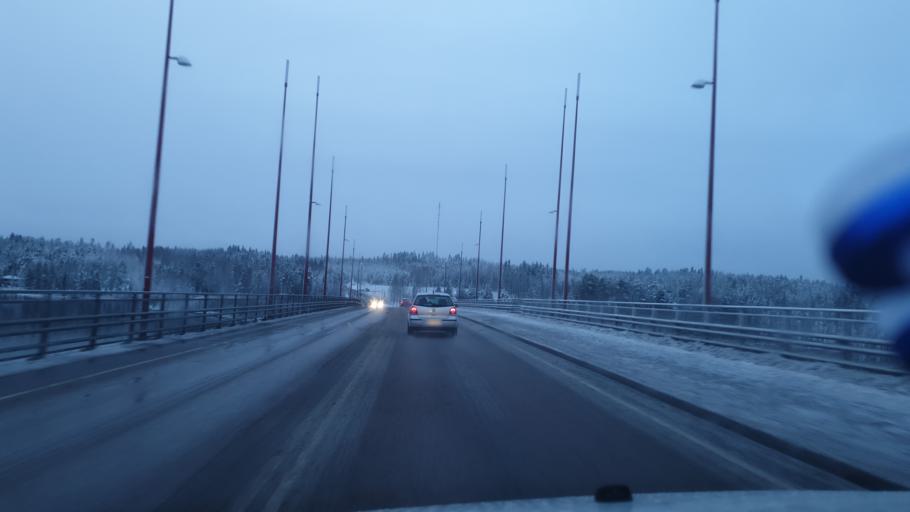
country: FI
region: Central Finland
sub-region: Saarijaervi-Viitasaari
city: Viitasaari
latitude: 63.0433
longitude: 25.8174
